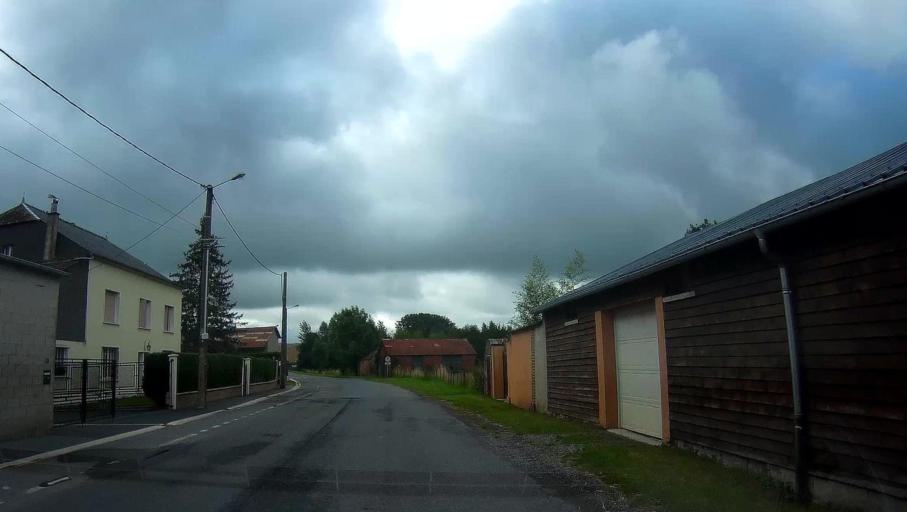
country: FR
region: Picardie
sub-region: Departement de l'Aisne
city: Rozoy-sur-Serre
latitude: 49.6894
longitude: 4.2502
